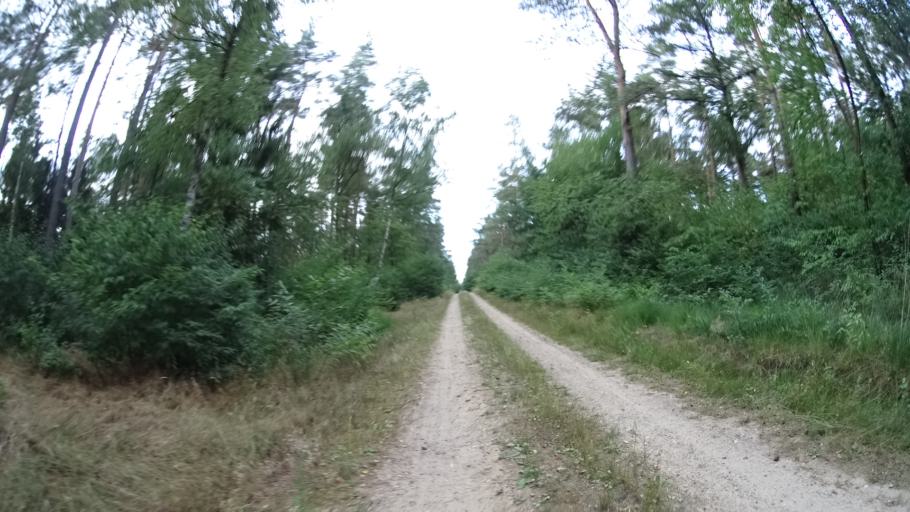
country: DE
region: Lower Saxony
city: Handeloh
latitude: 53.2042
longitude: 9.8798
